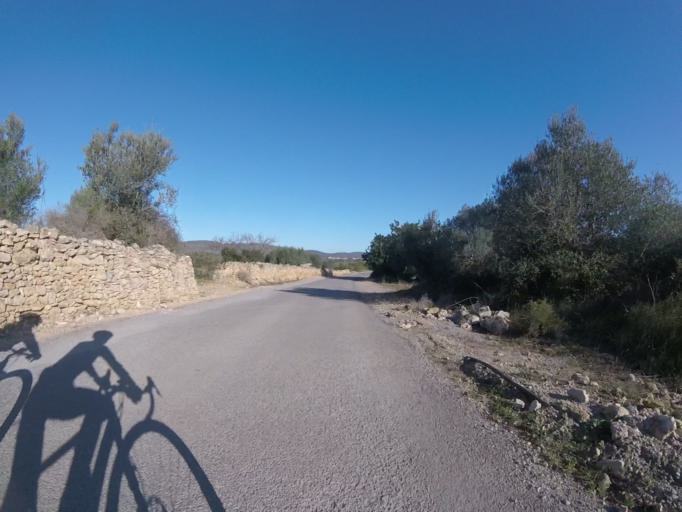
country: ES
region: Valencia
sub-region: Provincia de Castello
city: Alcala de Xivert
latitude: 40.2919
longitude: 0.2169
